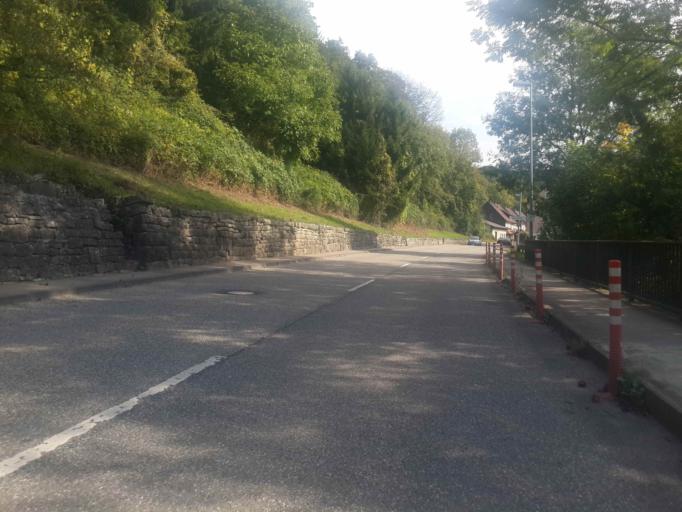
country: DE
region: Baden-Wuerttemberg
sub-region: Regierungsbezirk Stuttgart
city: Neudenau
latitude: 49.2920
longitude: 9.2758
